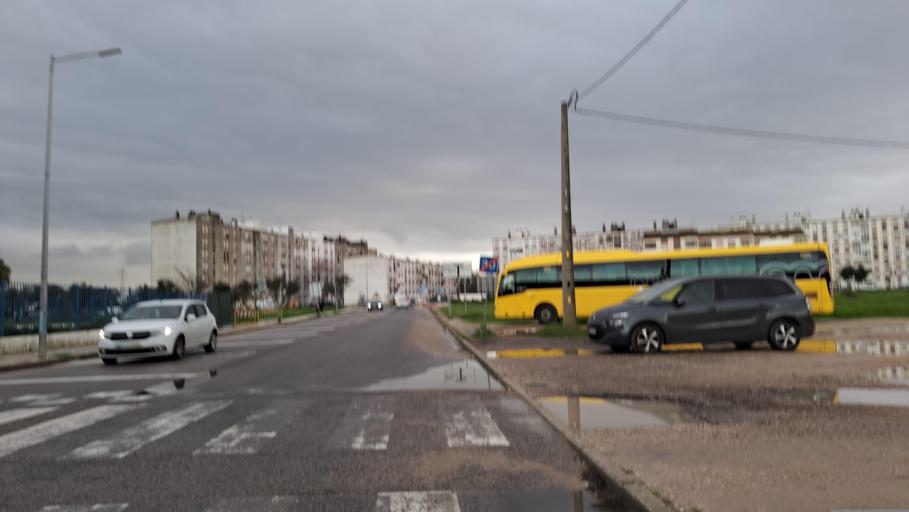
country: PT
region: Setubal
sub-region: Moita
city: Alhos Vedros
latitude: 38.6533
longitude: -9.0375
